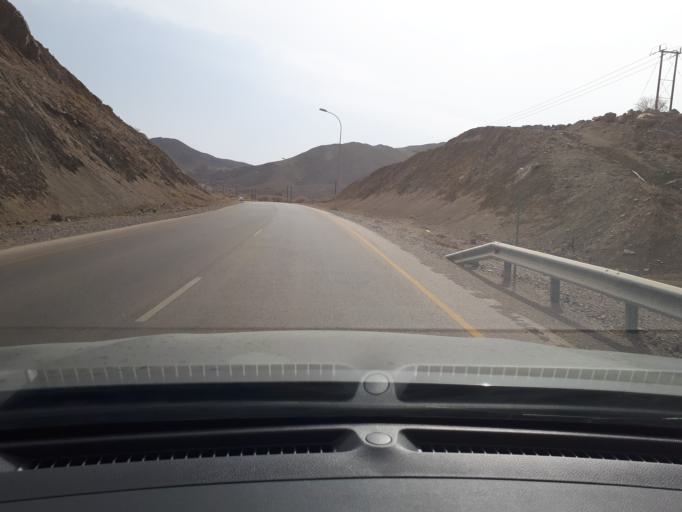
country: OM
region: Ash Sharqiyah
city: Badiyah
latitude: 22.5368
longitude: 58.9767
